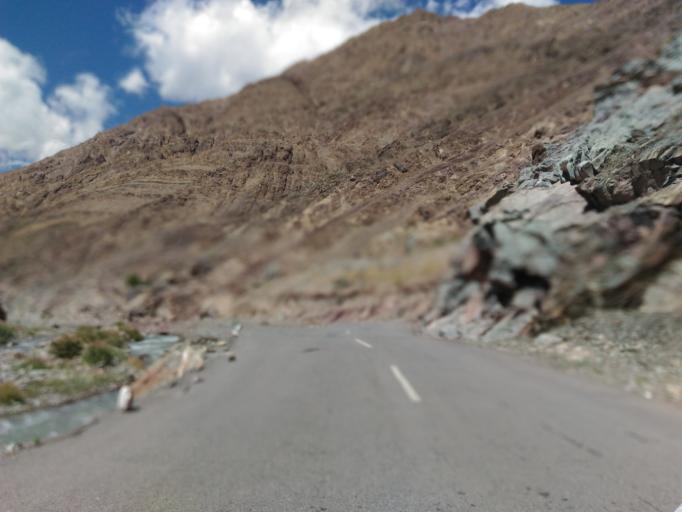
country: IN
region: Kashmir
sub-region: Ladakh
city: Leh
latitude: 33.8146
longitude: 77.8112
